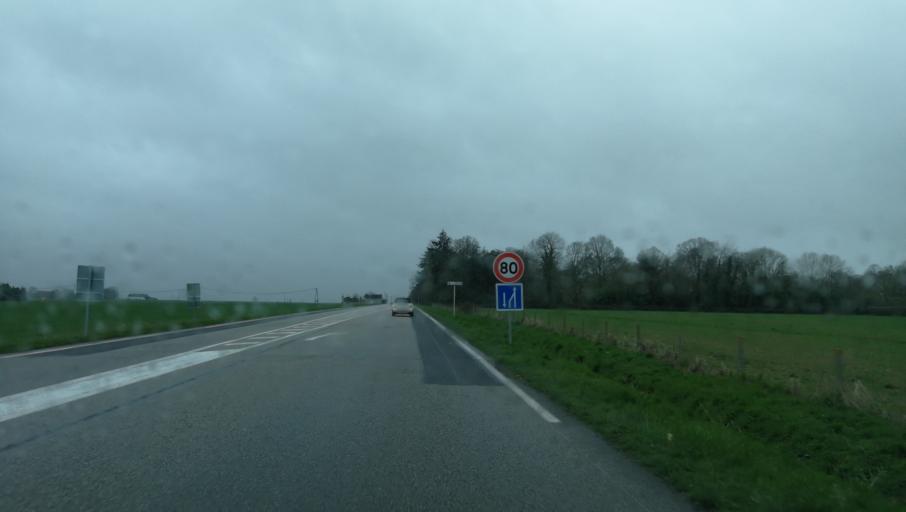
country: FR
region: Haute-Normandie
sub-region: Departement de l'Eure
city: Brionne
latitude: 49.1809
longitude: 0.7048
